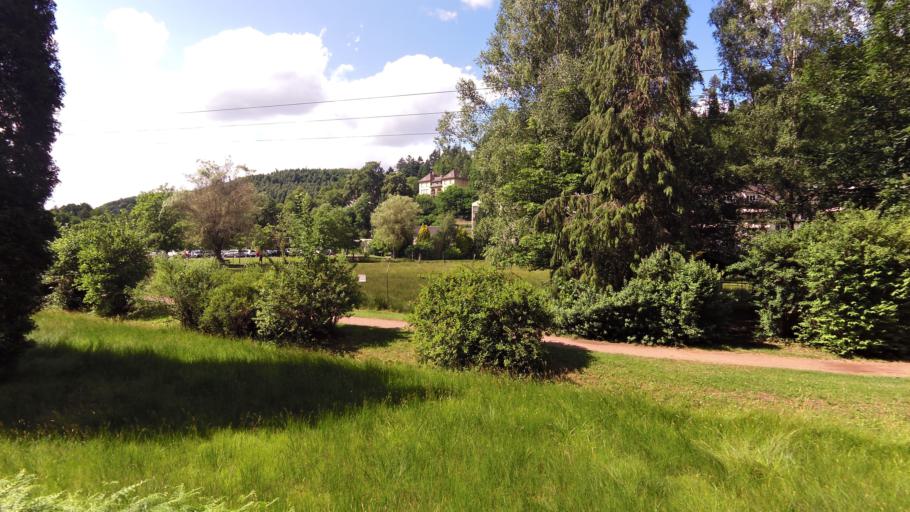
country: FR
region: Lorraine
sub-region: Departement de la Moselle
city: Abreschviller
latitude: 48.6272
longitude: 7.1223
